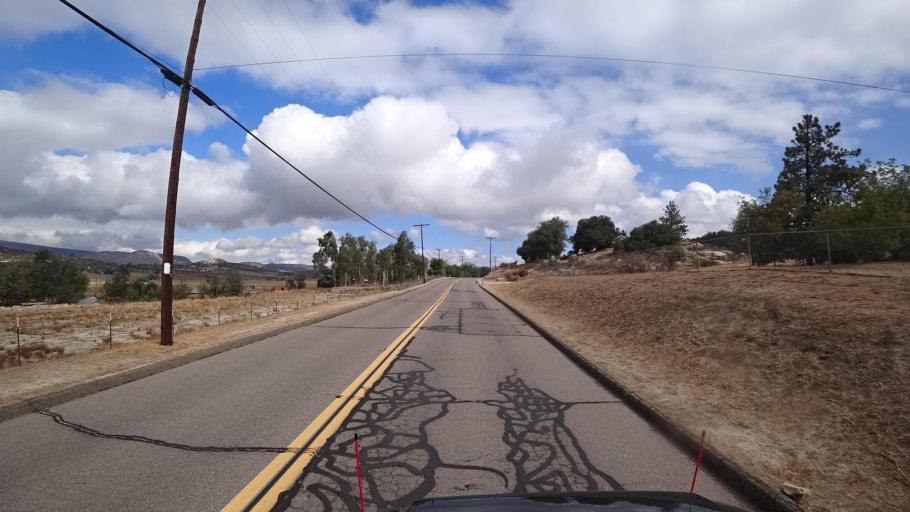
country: US
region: California
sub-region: San Diego County
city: Campo
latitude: 32.6126
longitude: -116.4702
